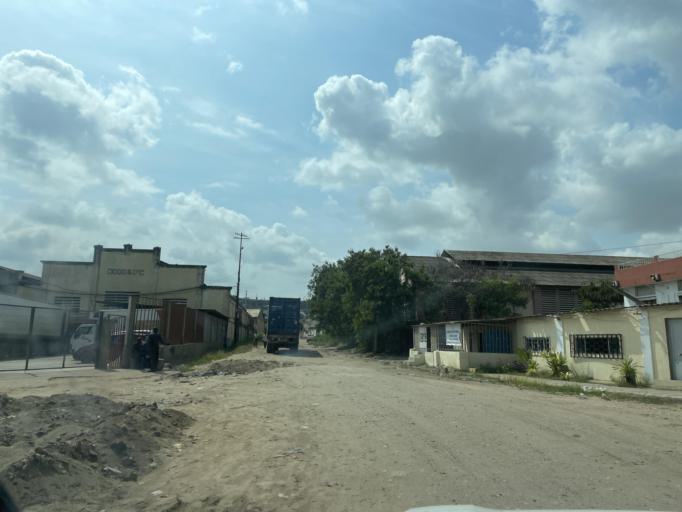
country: AO
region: Luanda
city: Luanda
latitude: -8.8030
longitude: 13.2553
